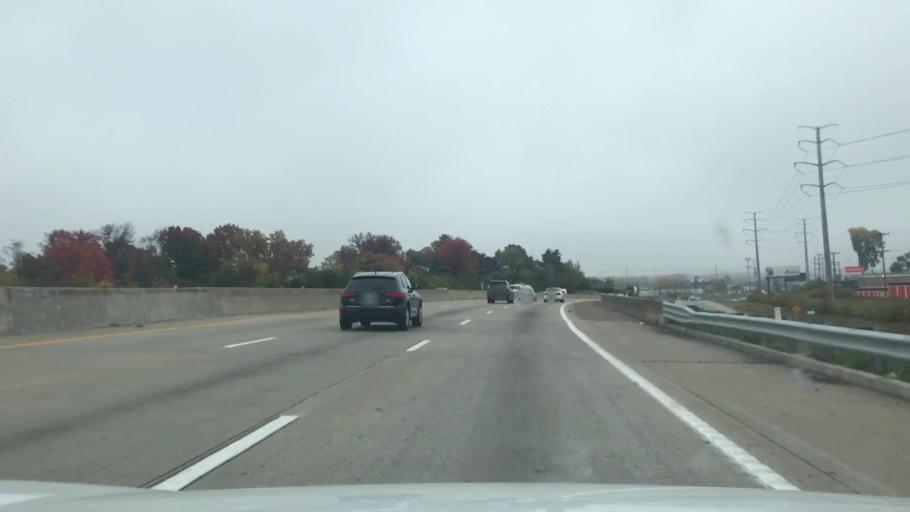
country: US
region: Missouri
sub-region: Saint Louis County
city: Olivette
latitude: 38.6737
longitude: -90.3620
